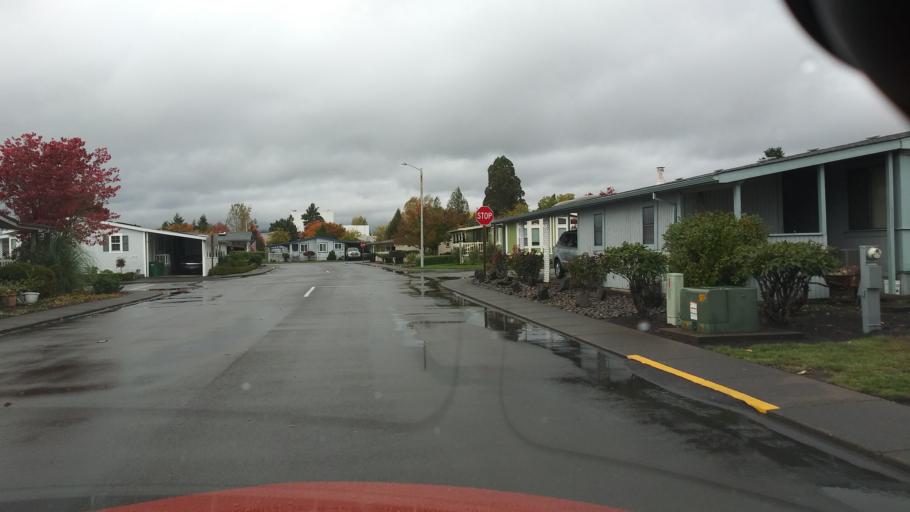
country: US
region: Oregon
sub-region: Washington County
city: Cornelius
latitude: 45.5131
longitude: -123.0727
